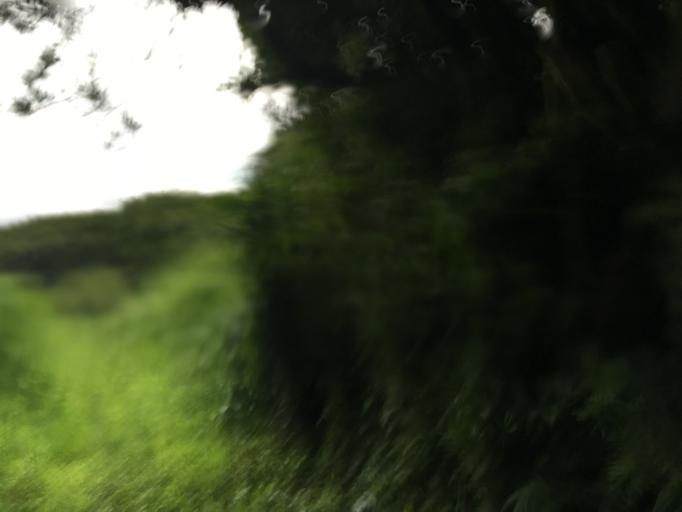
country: JP
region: Aichi
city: Ishiki
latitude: 34.7297
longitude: 137.0411
